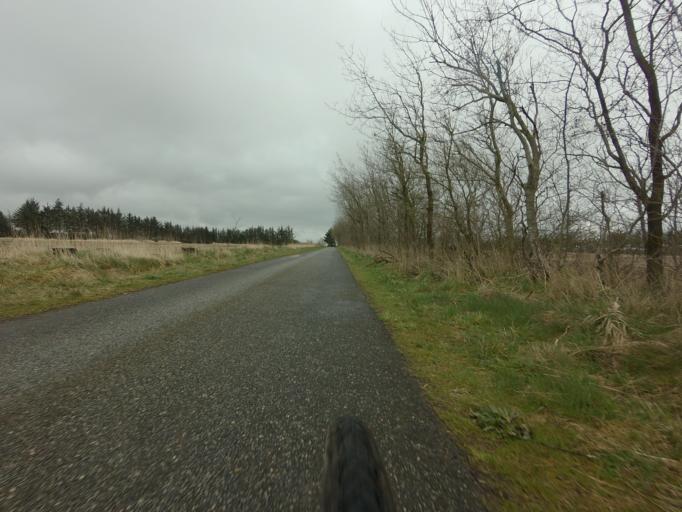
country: DK
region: North Denmark
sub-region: Jammerbugt Kommune
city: Pandrup
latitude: 57.3275
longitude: 9.7863
